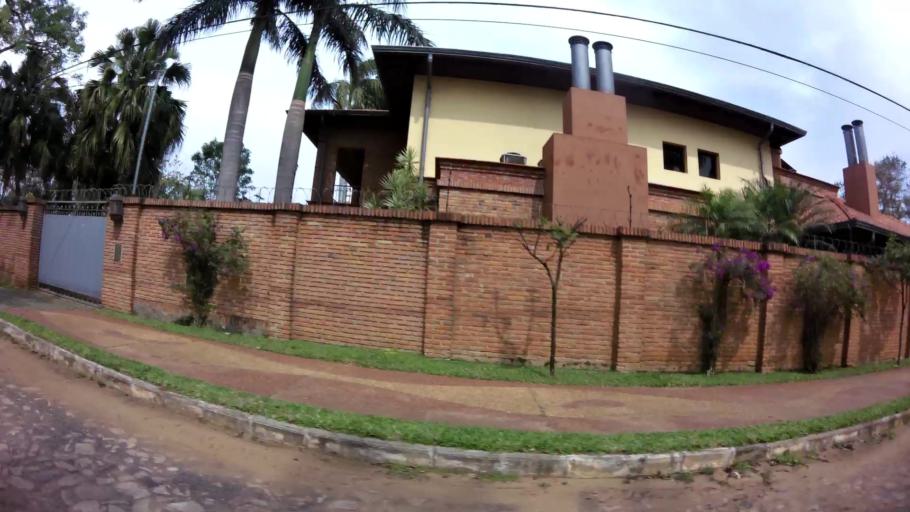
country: PY
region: Central
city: Fernando de la Mora
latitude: -25.2753
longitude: -57.5555
